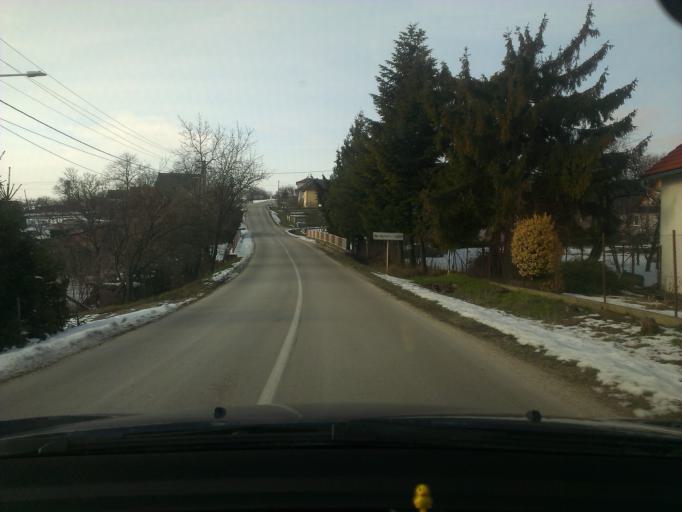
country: SK
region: Nitriansky
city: Stara Tura
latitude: 48.7353
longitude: 17.6573
